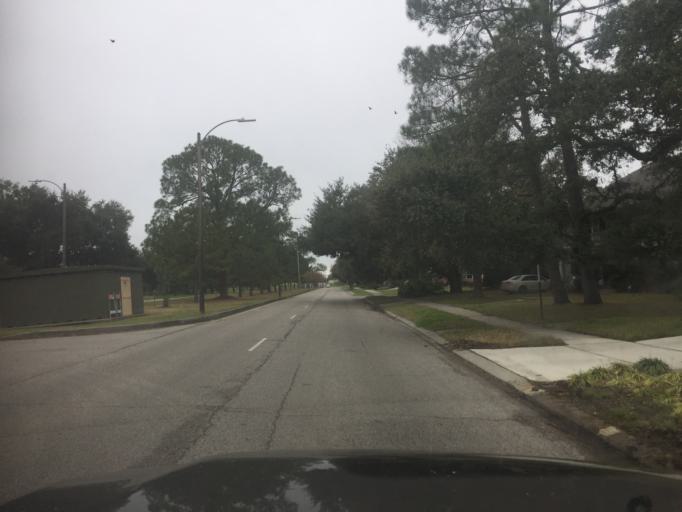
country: US
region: Louisiana
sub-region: Orleans Parish
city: New Orleans
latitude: 30.0186
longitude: -90.0935
